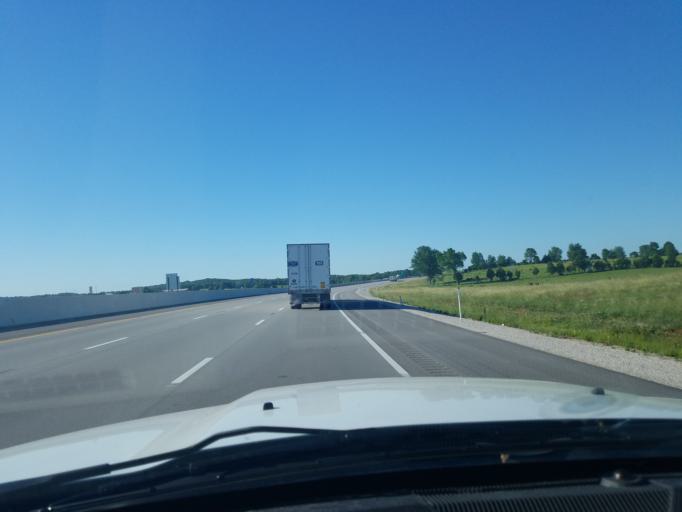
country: US
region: Kentucky
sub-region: Larue County
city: Hodgenville
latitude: 37.4930
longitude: -85.8812
